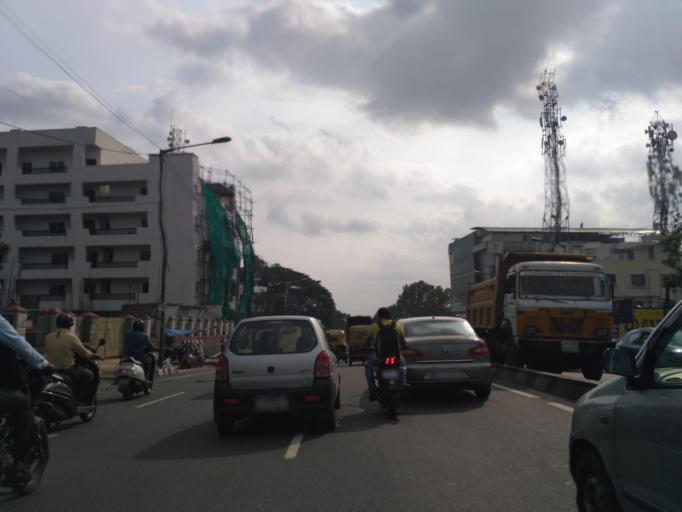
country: IN
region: Karnataka
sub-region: Bangalore Urban
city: Bangalore
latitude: 12.9568
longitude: 77.5499
